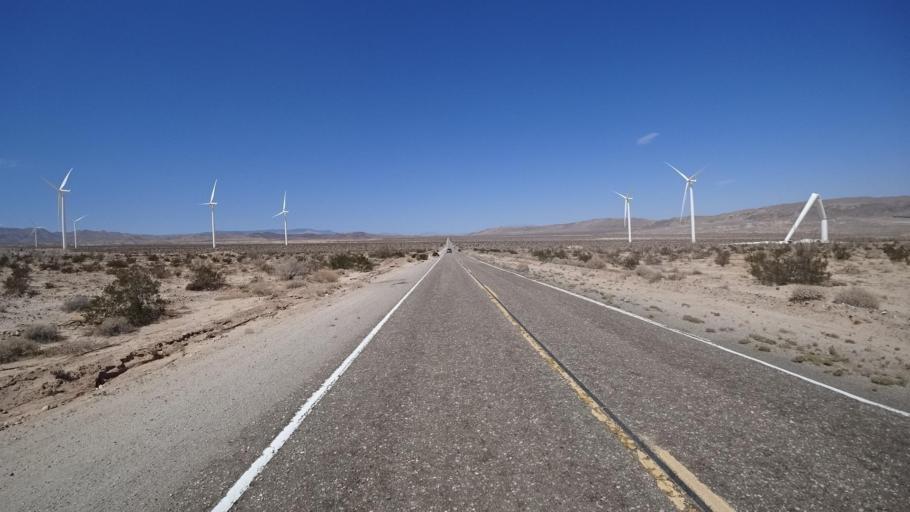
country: MX
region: Baja California
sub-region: Tecate
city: Cereso del Hongo
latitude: 32.7592
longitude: -116.0642
